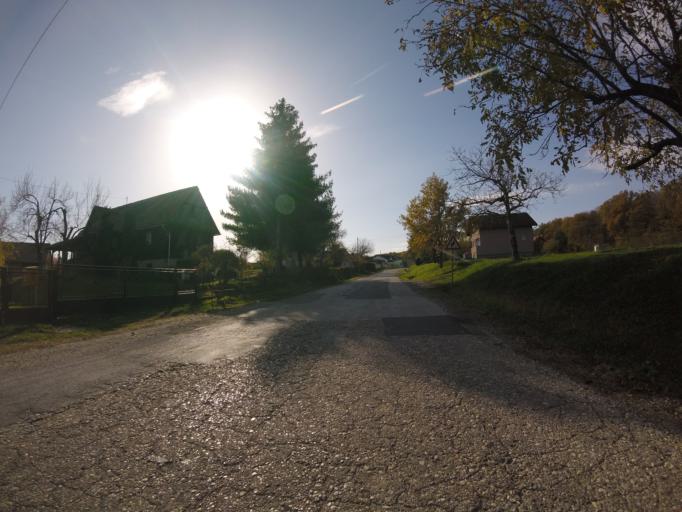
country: HR
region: Zagrebacka
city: Mraclin
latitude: 45.6128
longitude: 16.0730
